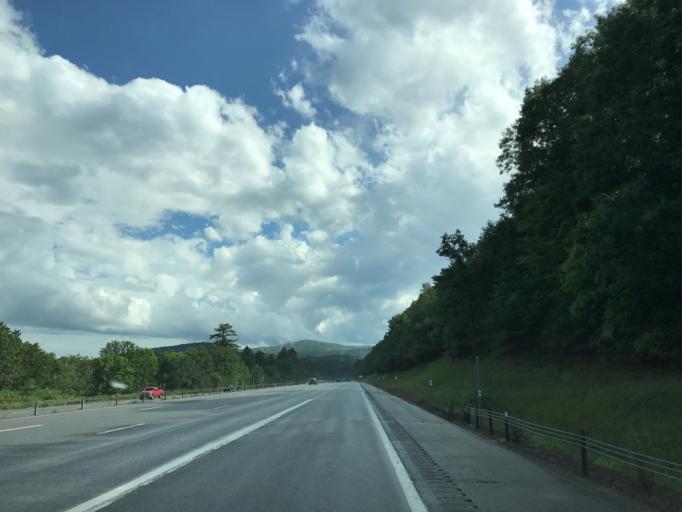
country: US
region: New York
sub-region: Warren County
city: Warrensburg
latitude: 43.4229
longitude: -73.7218
